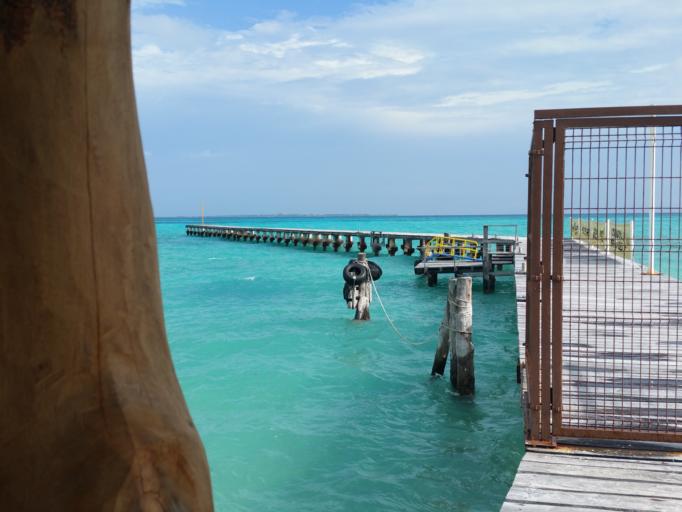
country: MX
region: Quintana Roo
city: Isla Mujeres
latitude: 21.1370
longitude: -86.7463
